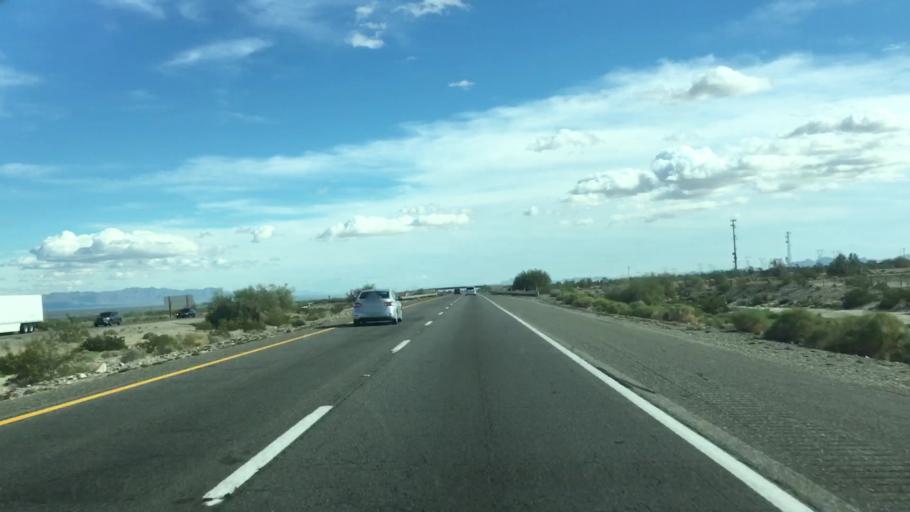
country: US
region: California
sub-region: Imperial County
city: Niland
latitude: 33.6857
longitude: -115.2549
